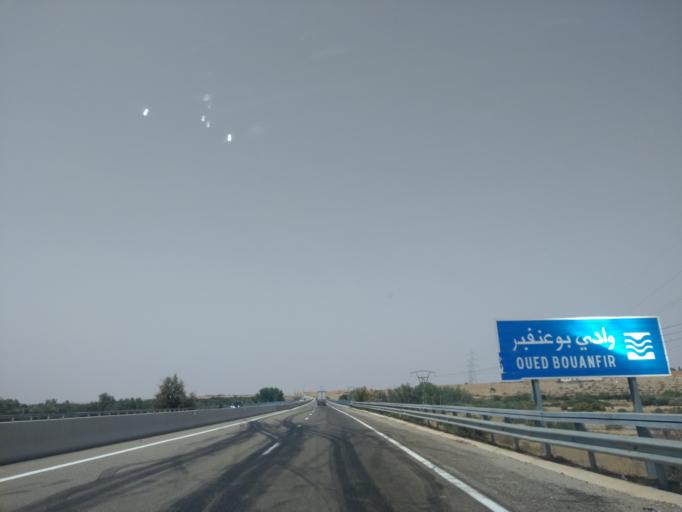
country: MA
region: Marrakech-Tensift-Al Haouz
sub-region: Chichaoua
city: Chichaoua
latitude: 31.3983
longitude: -8.7511
